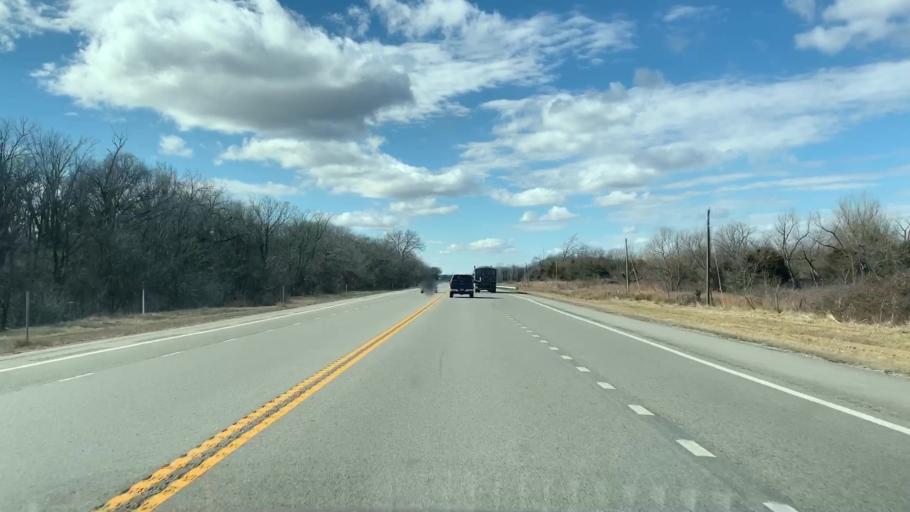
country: US
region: Kansas
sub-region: Cherokee County
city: Columbus
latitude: 37.3401
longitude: -94.9277
